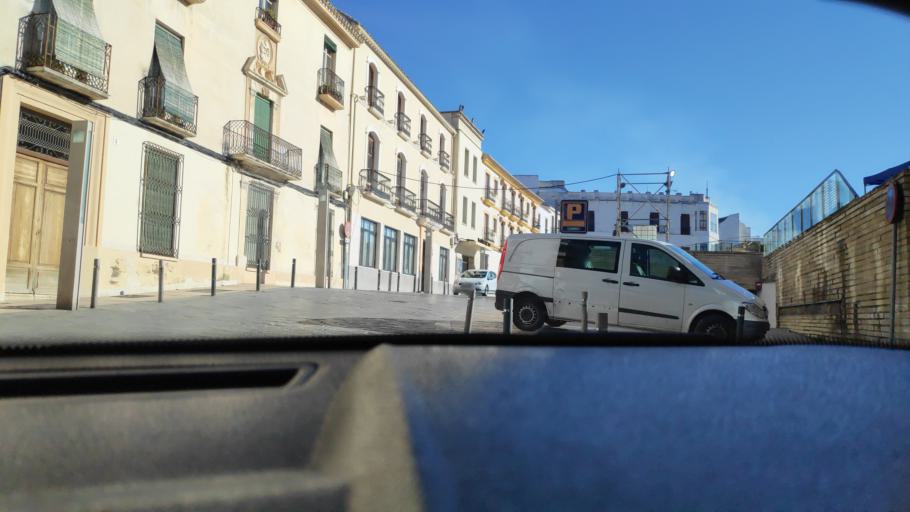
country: ES
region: Andalusia
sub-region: Province of Cordoba
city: Baena
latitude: 37.6146
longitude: -4.3263
